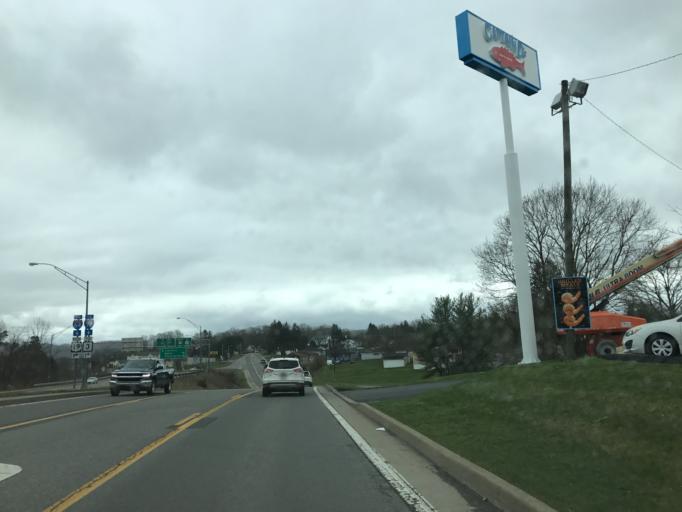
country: US
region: West Virginia
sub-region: Raleigh County
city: Beckley
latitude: 37.7727
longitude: -81.1609
